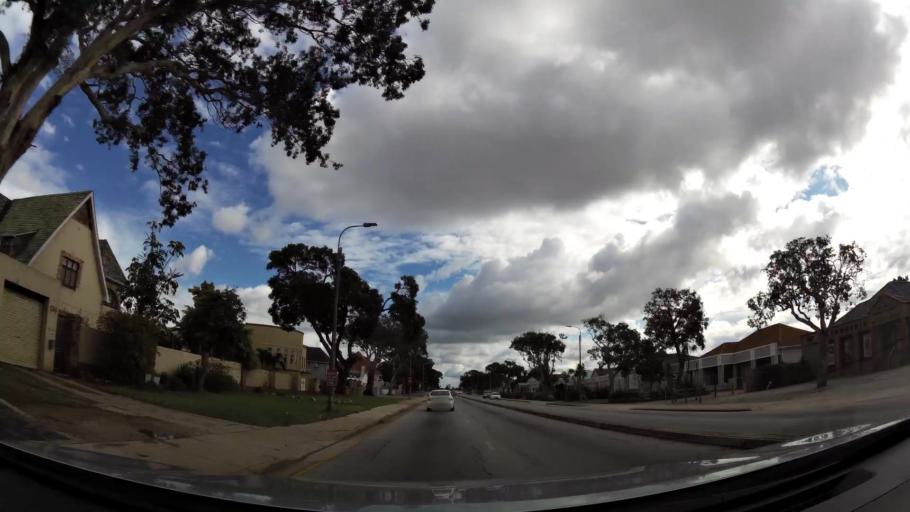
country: ZA
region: Eastern Cape
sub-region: Nelson Mandela Bay Metropolitan Municipality
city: Port Elizabeth
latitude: -33.9548
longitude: 25.5849
